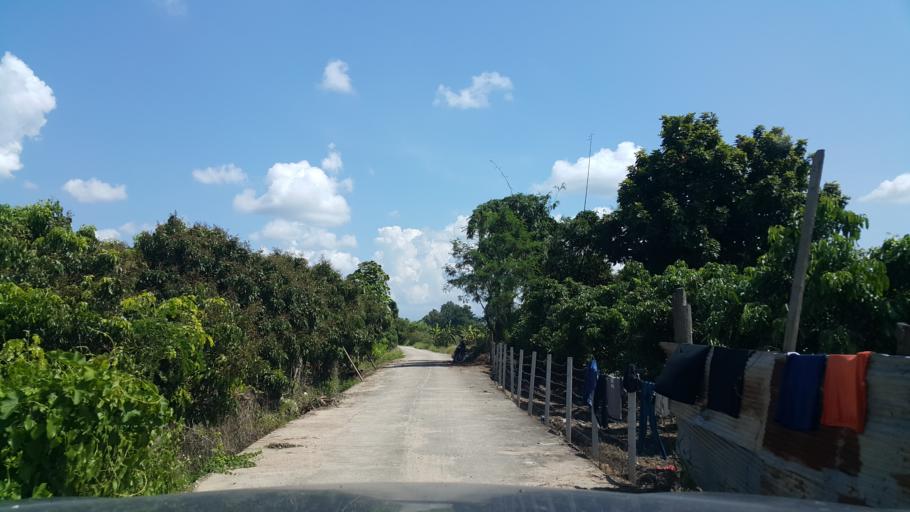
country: TH
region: Chiang Mai
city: Chom Thong
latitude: 18.4170
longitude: 98.6857
